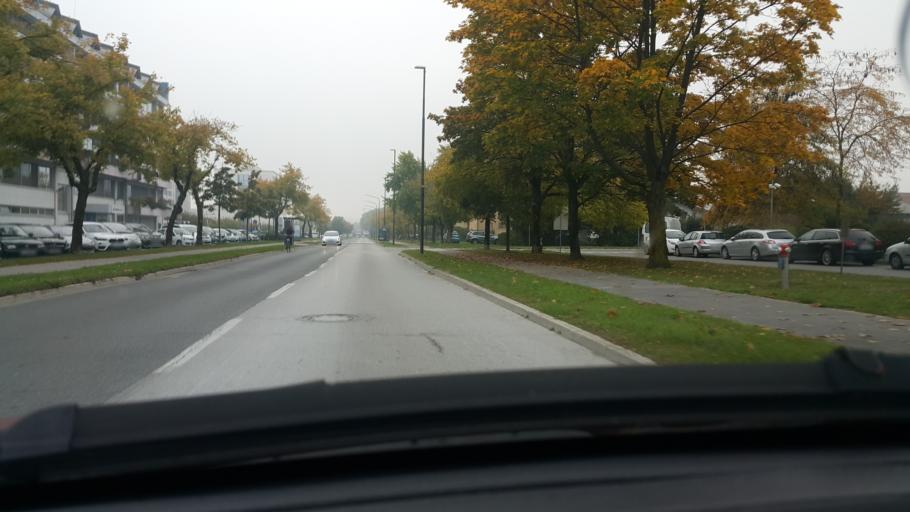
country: SI
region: Ljubljana
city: Ljubljana
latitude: 46.0769
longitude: 14.5005
